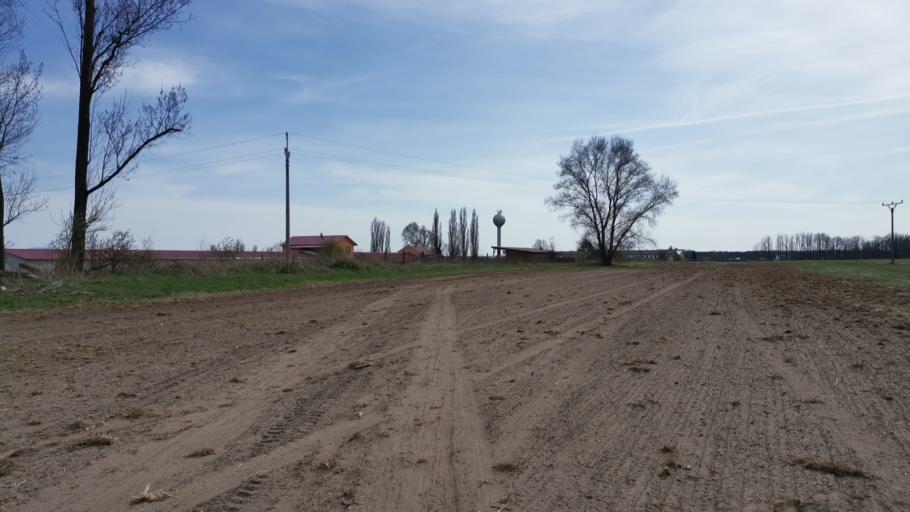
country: SK
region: Trnavsky
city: Gbely
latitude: 48.6616
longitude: 17.0990
